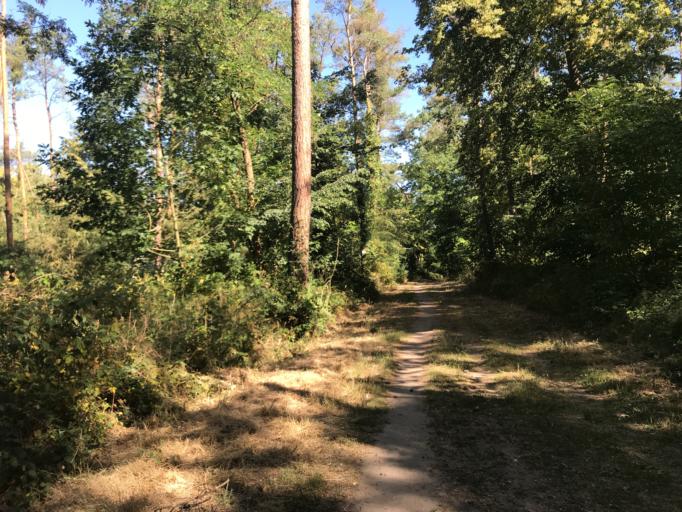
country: DE
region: Rheinland-Pfalz
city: Budenheim
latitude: 50.0096
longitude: 8.1459
